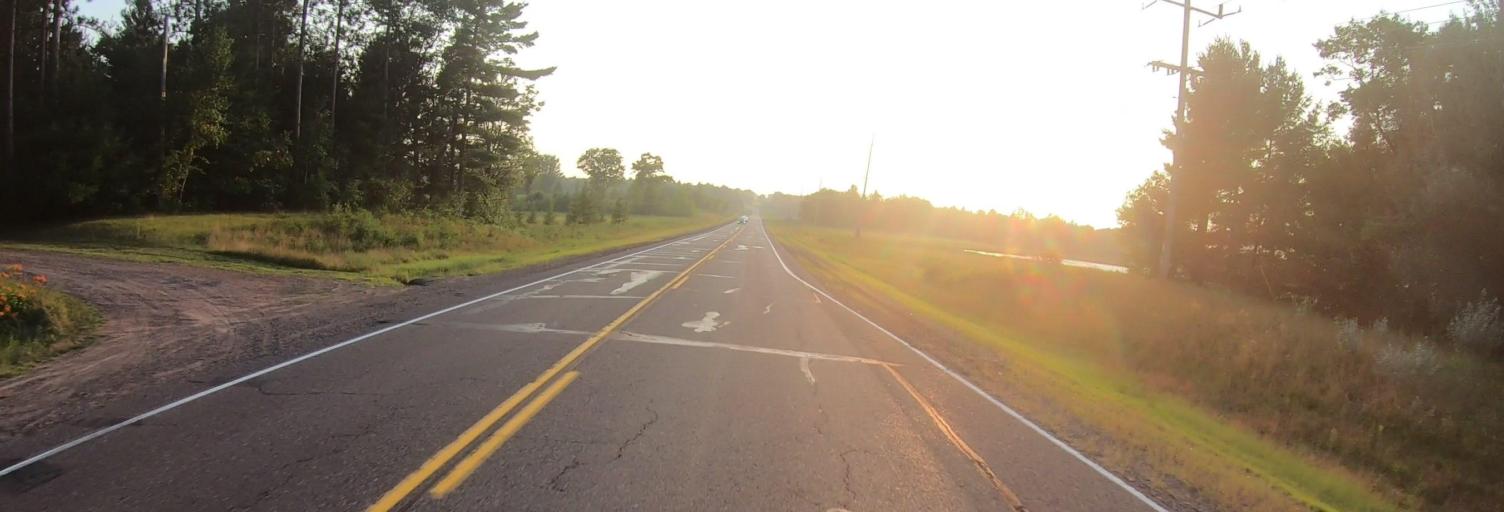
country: US
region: Wisconsin
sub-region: Burnett County
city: Siren
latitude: 45.7844
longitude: -92.4065
